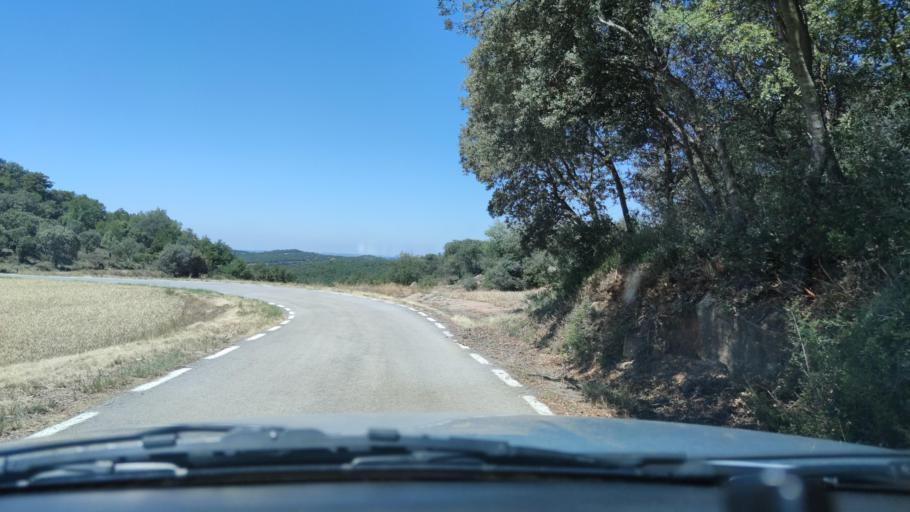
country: ES
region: Catalonia
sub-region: Provincia de Lleida
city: Tora de Riubregos
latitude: 41.8695
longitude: 1.4335
